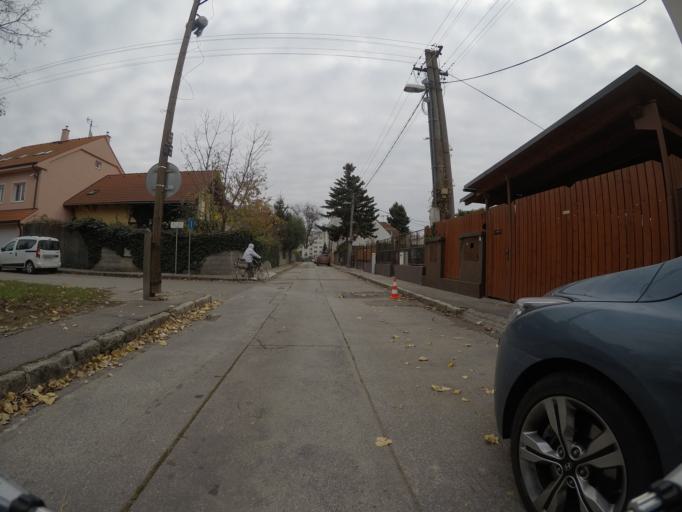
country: SK
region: Bratislavsky
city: Bratislava
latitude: 48.1734
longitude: 17.1695
